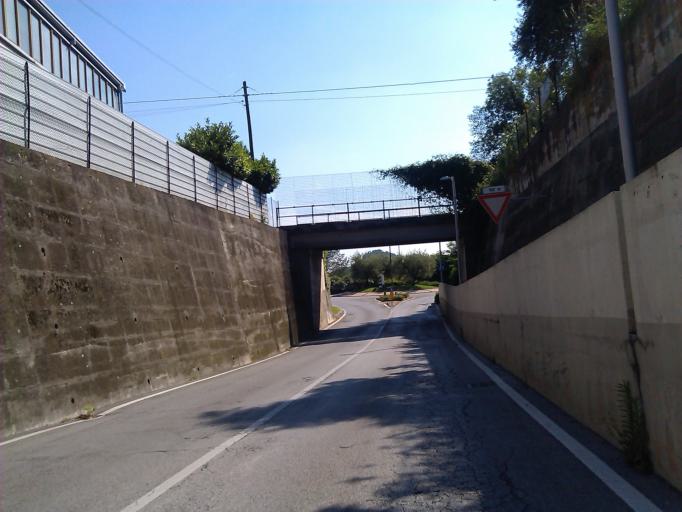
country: IT
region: Veneto
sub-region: Provincia di Vicenza
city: Pove del Grappa
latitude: 45.7896
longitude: 11.7320
